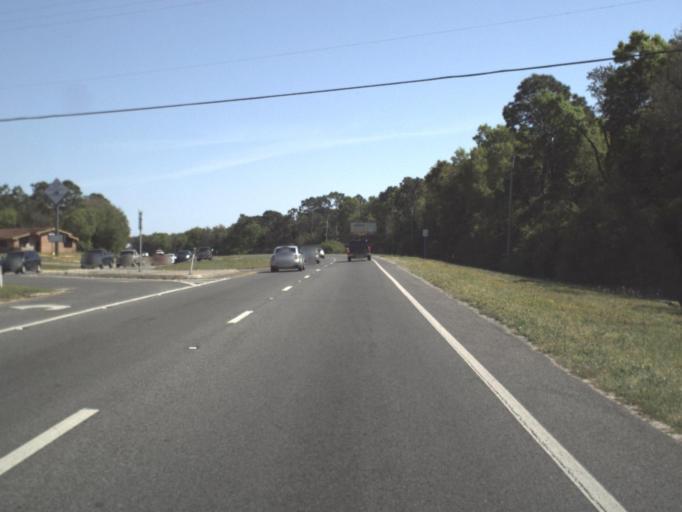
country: US
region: Florida
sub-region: Escambia County
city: Bellview
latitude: 30.4578
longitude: -87.2994
